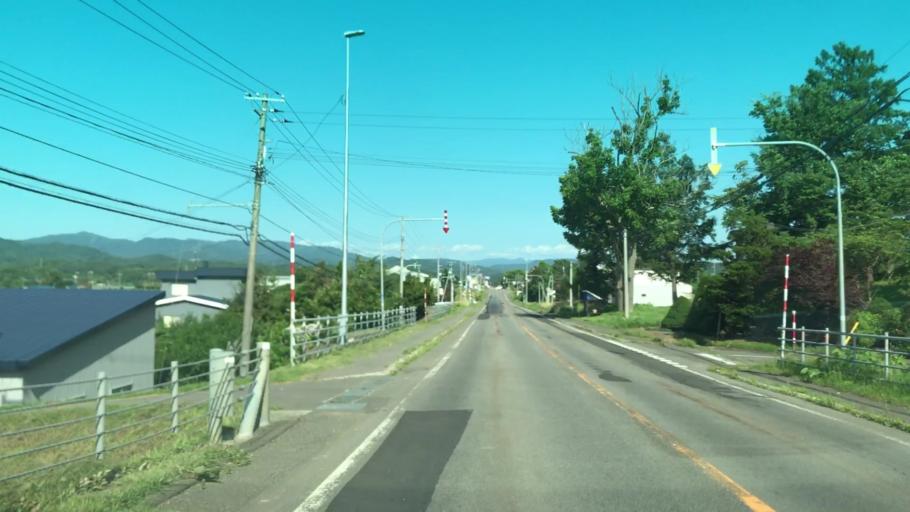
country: JP
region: Hokkaido
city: Iwanai
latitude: 42.9801
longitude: 140.6001
